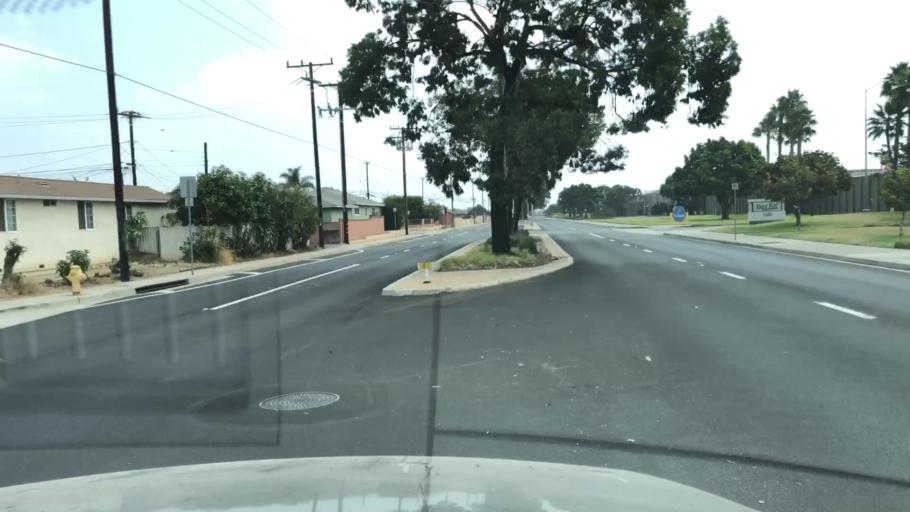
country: US
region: California
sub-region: Ventura County
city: Oxnard
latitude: 34.2004
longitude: -119.1665
